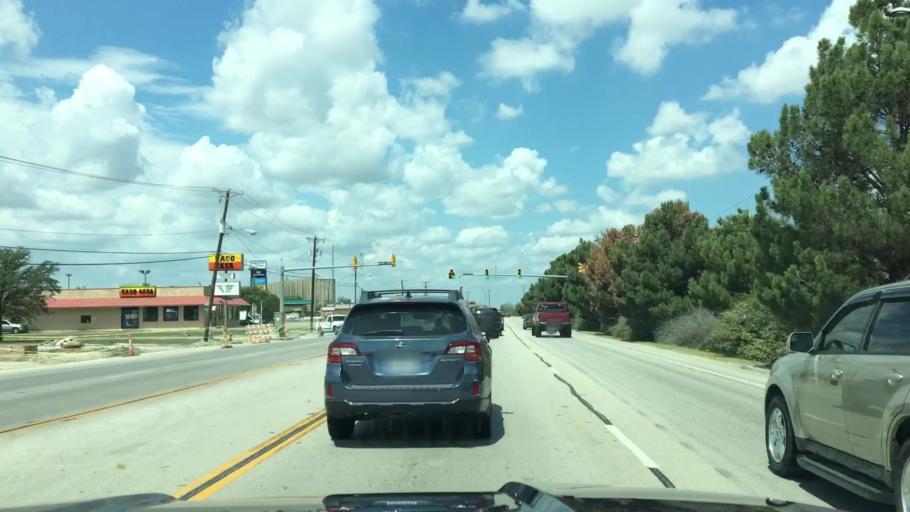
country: US
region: Texas
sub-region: Tarrant County
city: Saginaw
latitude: 32.8529
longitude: -97.3607
